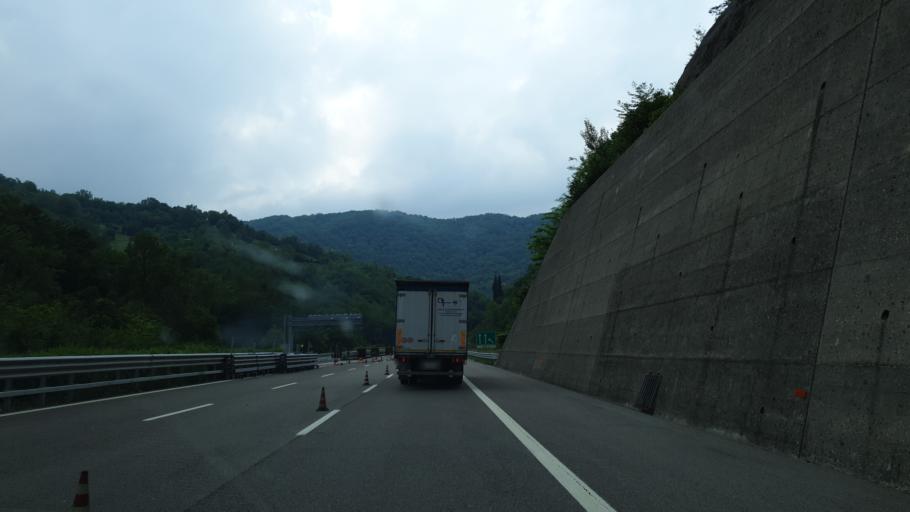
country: IT
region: Veneto
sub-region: Provincia di Treviso
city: Vittorio Veneto
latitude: 45.9800
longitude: 12.2804
